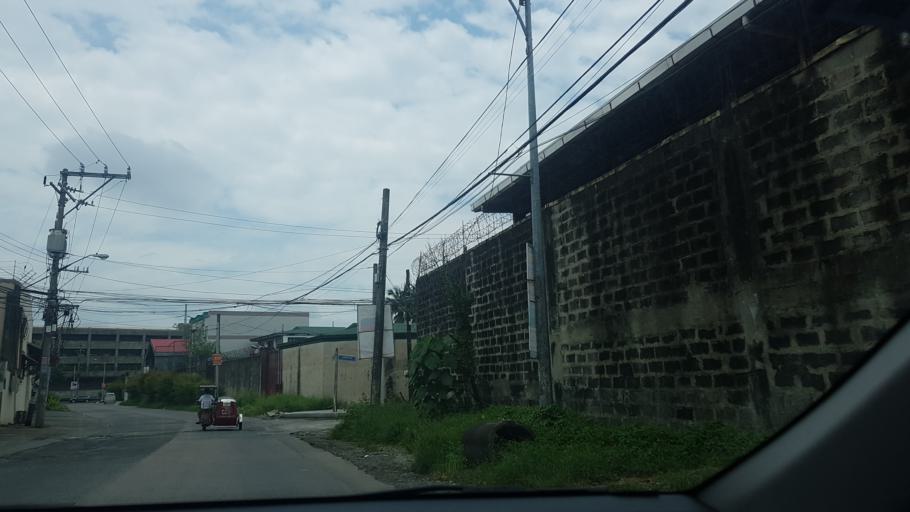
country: PH
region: Calabarzon
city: Del Monte
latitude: 14.6476
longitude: 121.0050
